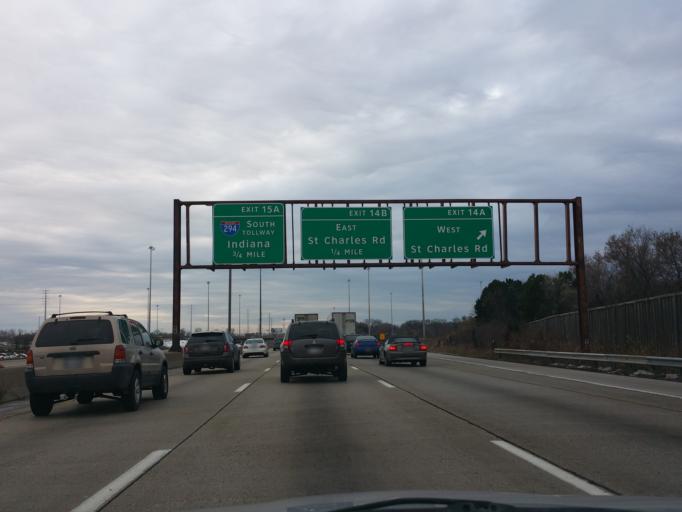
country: US
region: Illinois
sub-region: Cook County
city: Berkeley
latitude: 41.8941
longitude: -87.9206
